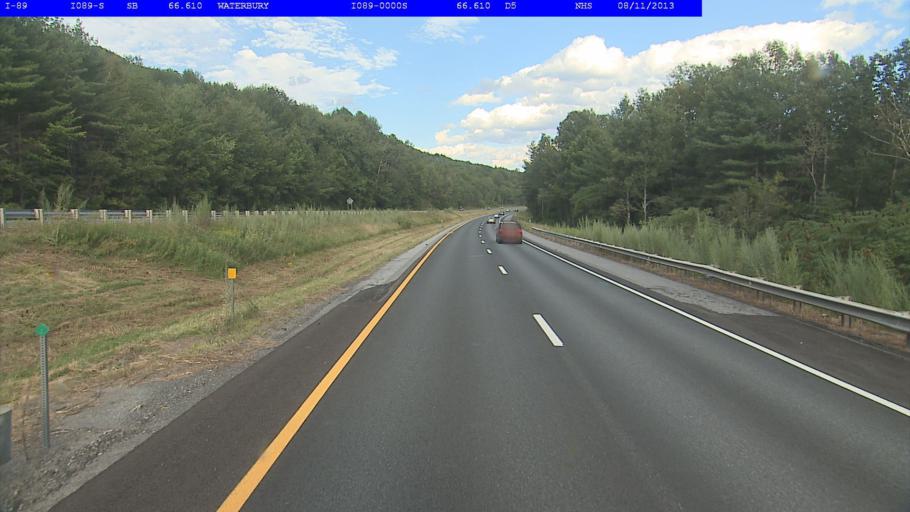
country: US
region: Vermont
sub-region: Washington County
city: Waterbury
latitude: 44.3609
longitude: -72.8024
